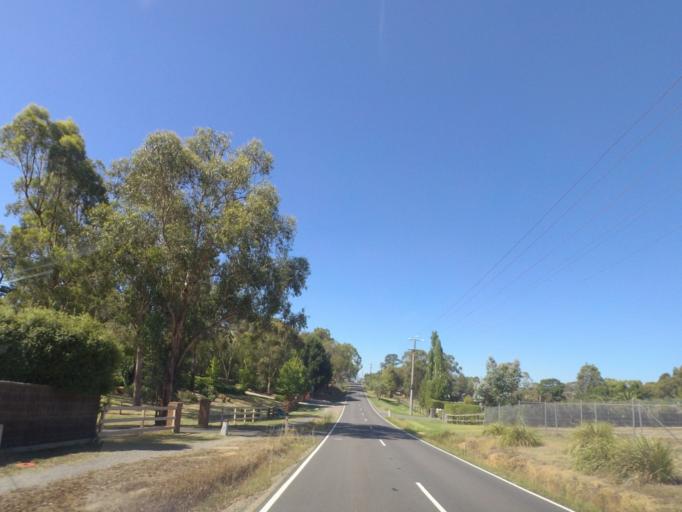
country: AU
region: Victoria
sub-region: Yarra Ranges
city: Chirnside Park
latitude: -37.7409
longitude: 145.2801
